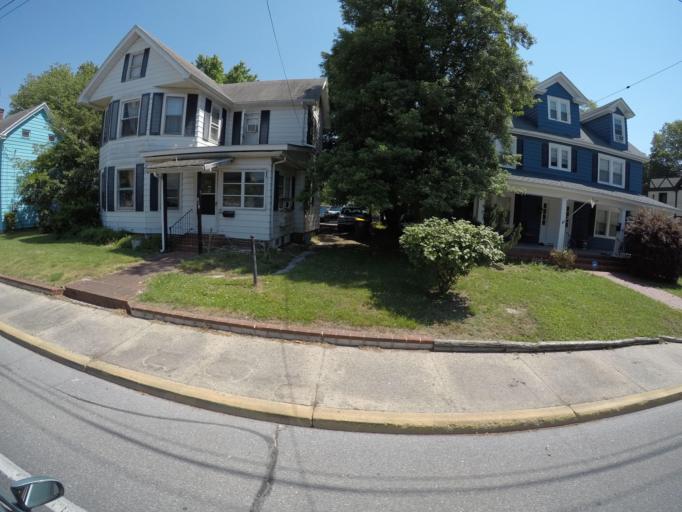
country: US
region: Delaware
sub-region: Sussex County
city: Georgetown
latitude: 38.6874
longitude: -75.3824
